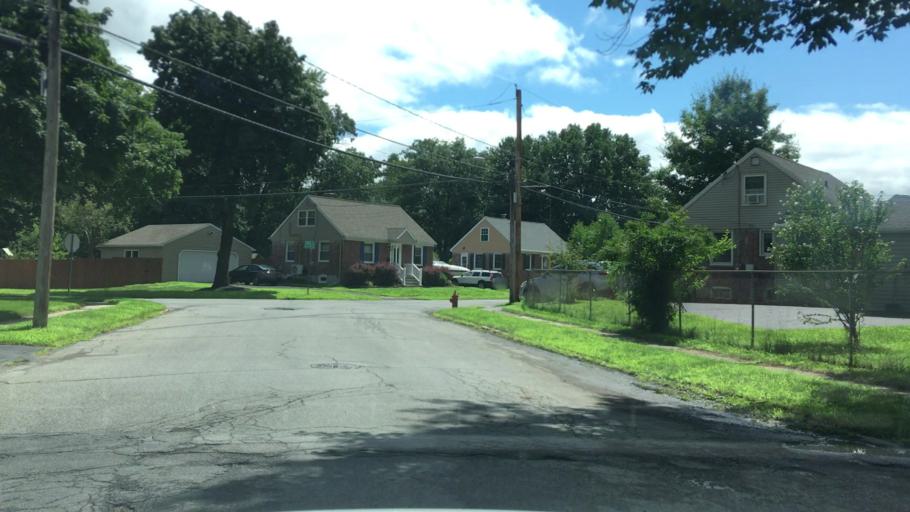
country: US
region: New York
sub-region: Albany County
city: Colonie
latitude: 42.7435
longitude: -73.8578
